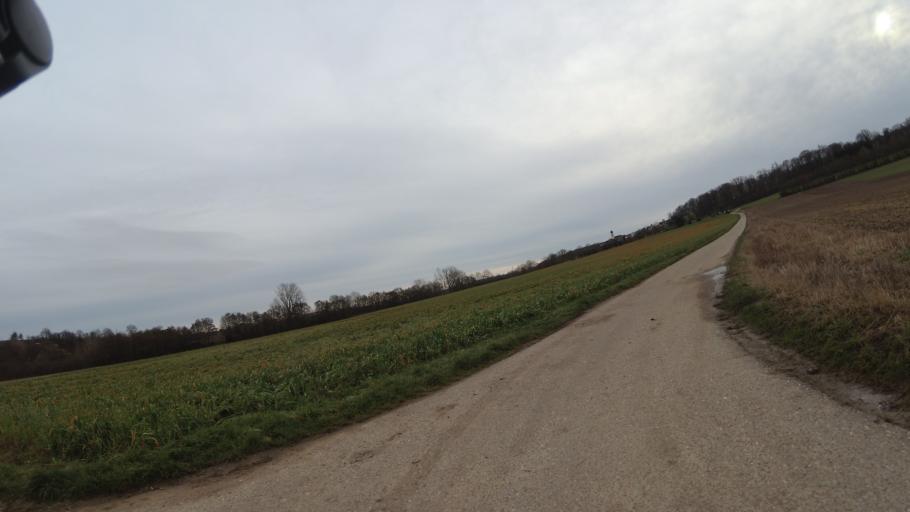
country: DE
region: Baden-Wuerttemberg
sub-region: Regierungsbezirk Stuttgart
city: Oedheim
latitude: 49.2586
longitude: 9.2832
